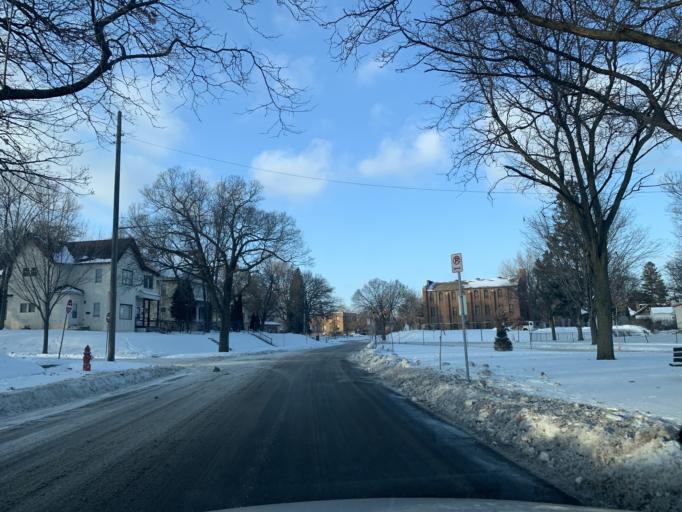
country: US
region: Minnesota
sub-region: Hennepin County
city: Minneapolis
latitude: 44.9855
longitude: -93.3010
